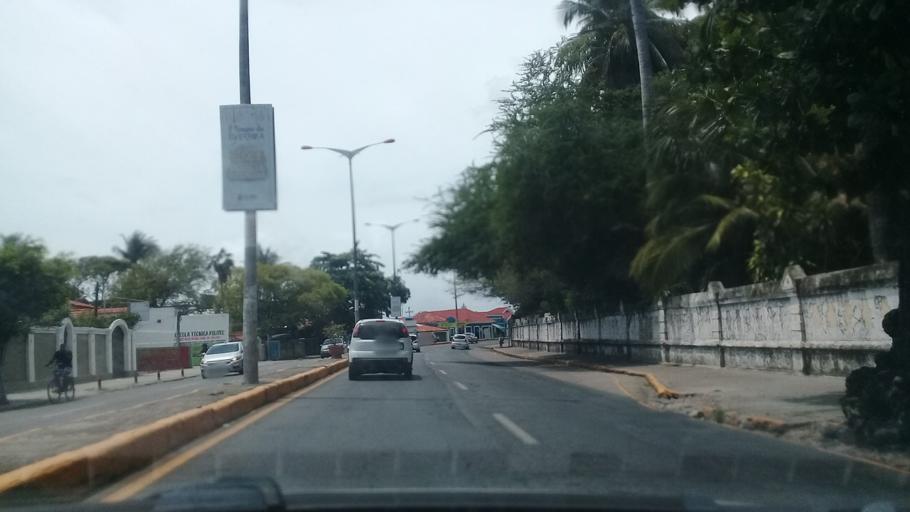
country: BR
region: Pernambuco
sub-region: Olinda
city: Olinda
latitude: -8.0205
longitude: -34.8515
